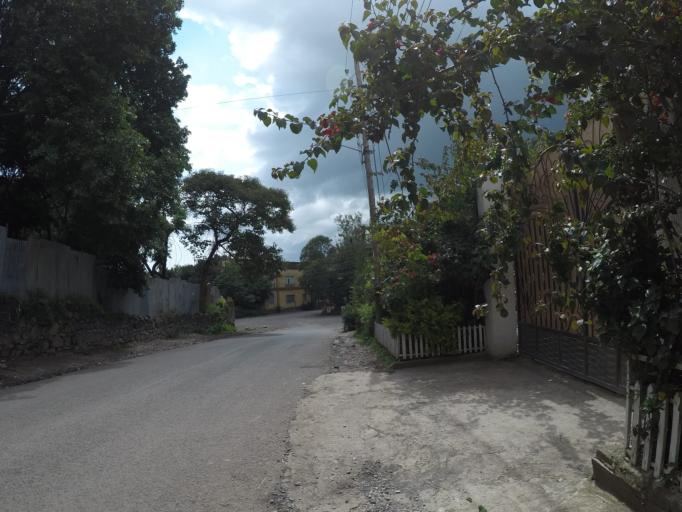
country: ET
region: Amhara
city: Gondar
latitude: 12.6146
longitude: 37.4741
